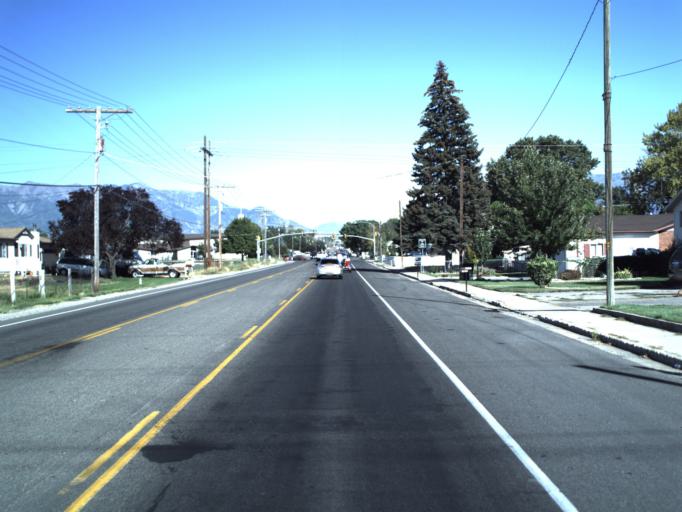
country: US
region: Utah
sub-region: Davis County
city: Clinton
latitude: 41.1398
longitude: -112.0576
